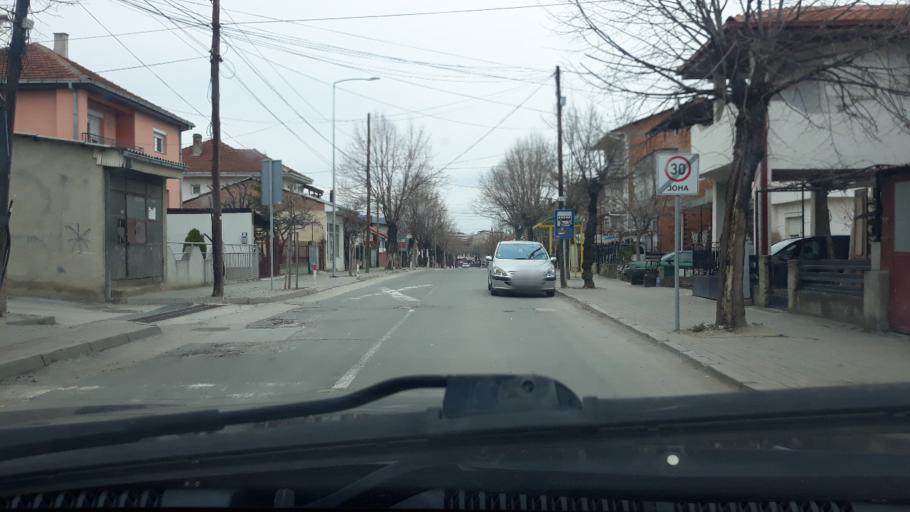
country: MK
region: Kavadarci
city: Kavadarci
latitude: 41.4316
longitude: 22.0087
